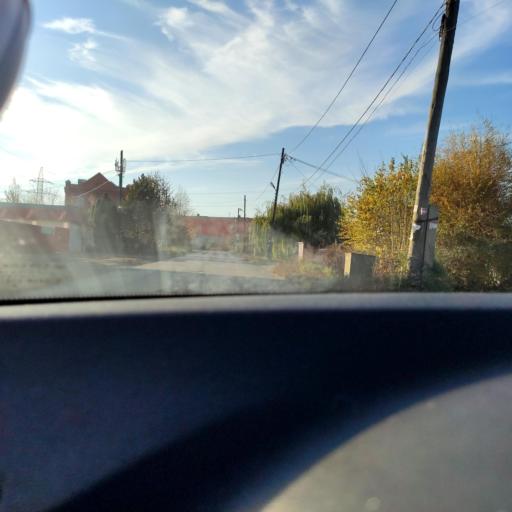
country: RU
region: Samara
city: Petra-Dubrava
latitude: 53.2549
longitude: 50.3144
